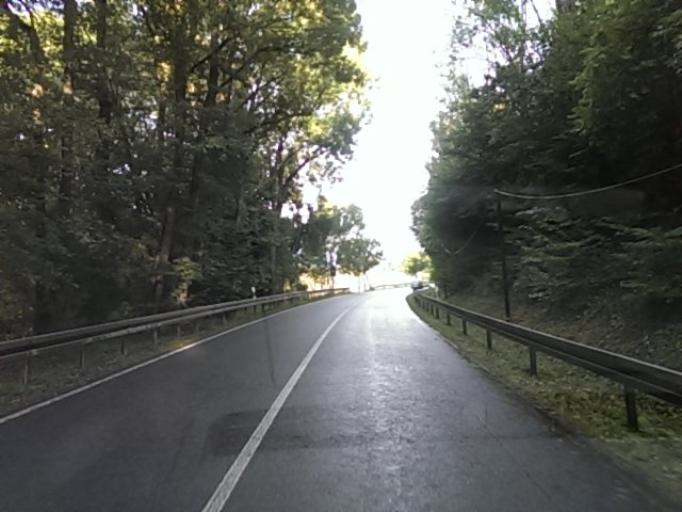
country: DE
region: Thuringia
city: Rastenberg
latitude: 51.1959
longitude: 11.3920
